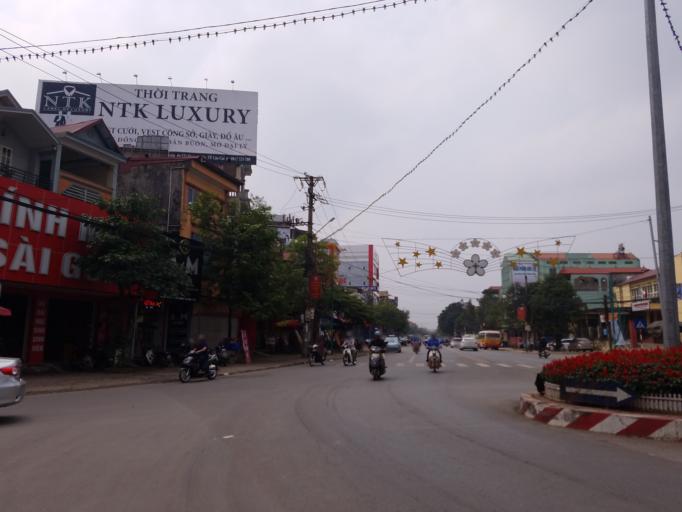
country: VN
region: Thai Nguyen
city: Thanh Pho Thai Nguyen
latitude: 21.6009
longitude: 105.8241
